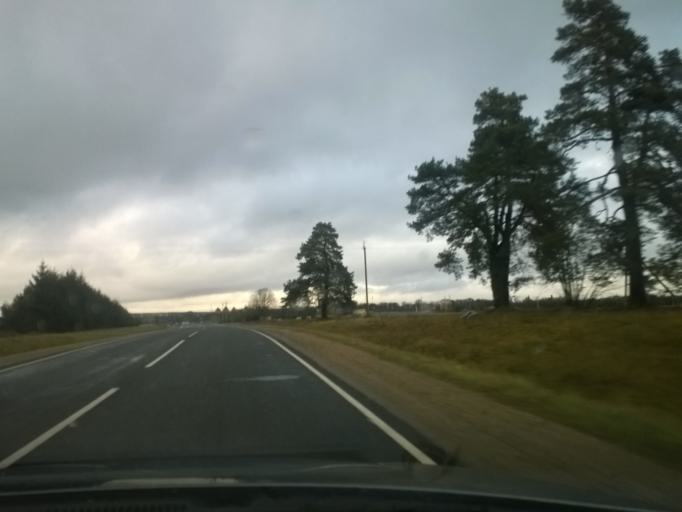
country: BY
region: Grodnenskaya
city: Mir
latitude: 53.4407
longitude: 26.4783
